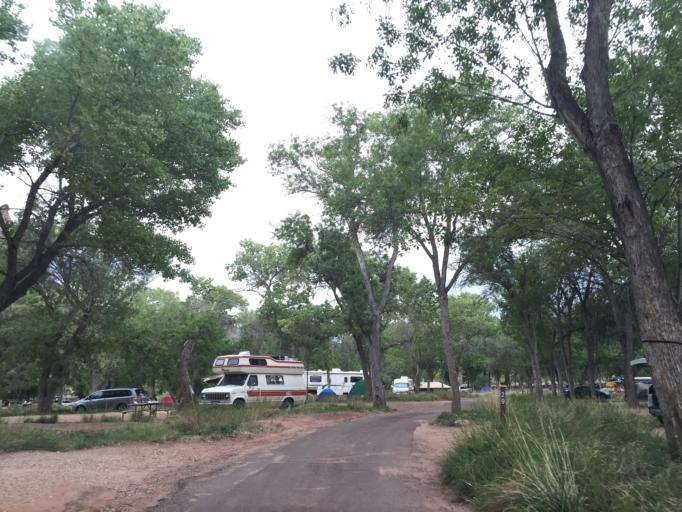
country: US
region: Utah
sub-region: Washington County
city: Hildale
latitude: 37.2033
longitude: -112.9856
